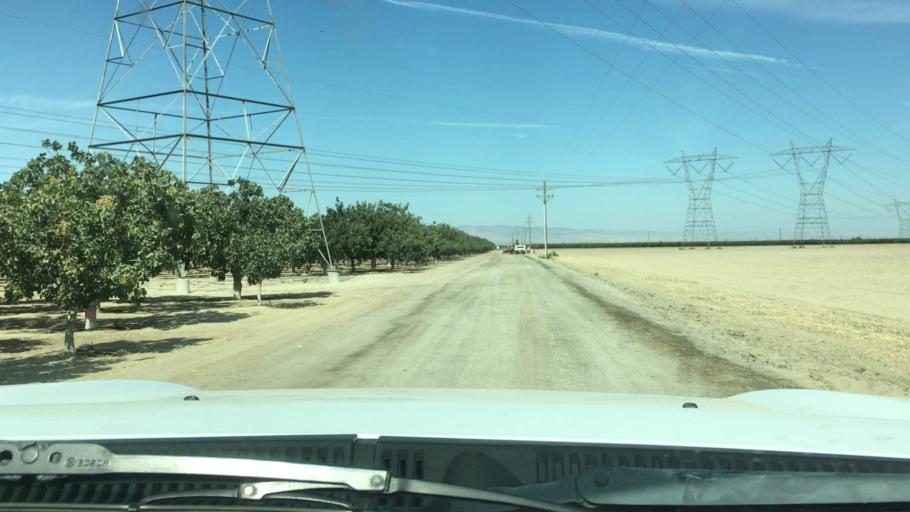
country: US
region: California
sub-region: Kern County
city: Buttonwillow
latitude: 35.3766
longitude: -119.3968
